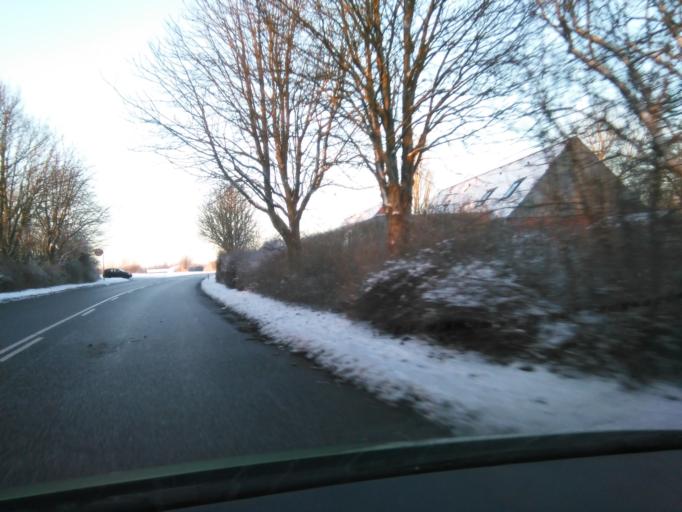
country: DK
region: Central Jutland
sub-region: Arhus Kommune
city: Kolt
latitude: 56.1080
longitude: 10.0679
